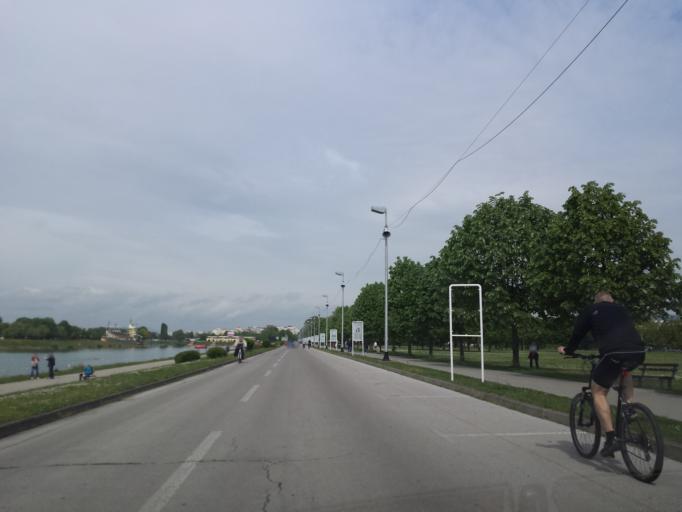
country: HR
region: Grad Zagreb
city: Jankomir
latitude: 45.7834
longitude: 15.9221
